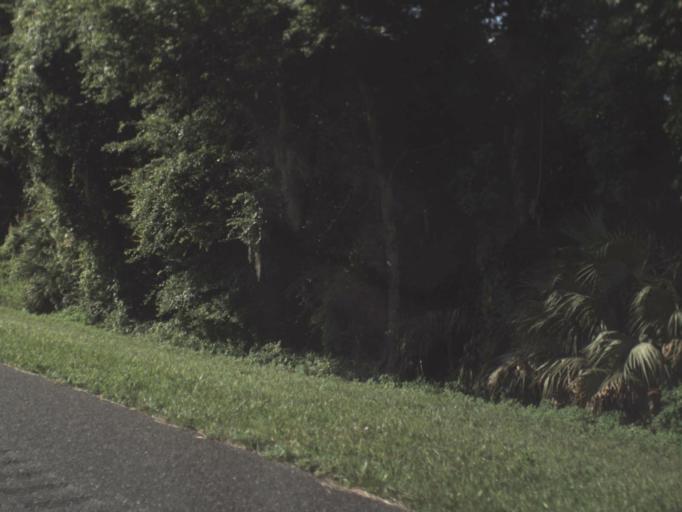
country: US
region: Florida
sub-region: Alachua County
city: Gainesville
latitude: 29.5391
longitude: -82.3125
